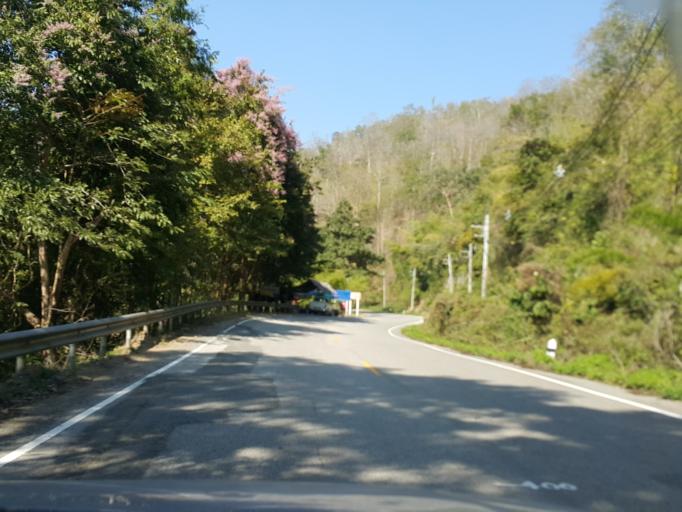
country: TH
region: Chiang Mai
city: Mae Wang
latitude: 18.6270
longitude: 98.7146
